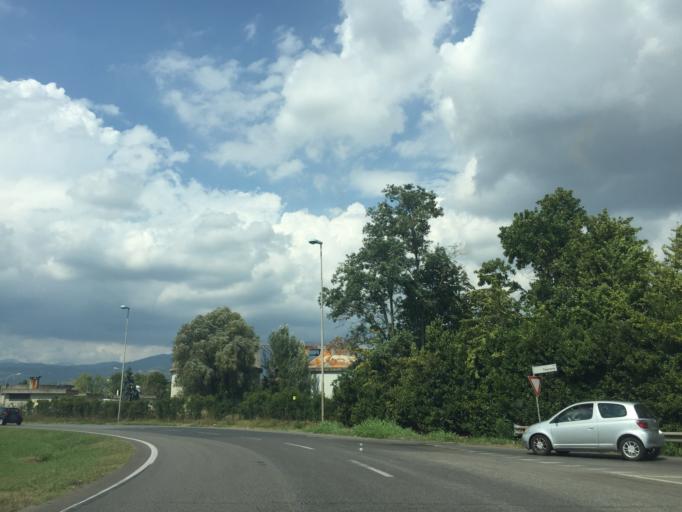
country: IT
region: Tuscany
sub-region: Provincia di Pistoia
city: Pistoia
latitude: 43.9234
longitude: 10.9334
